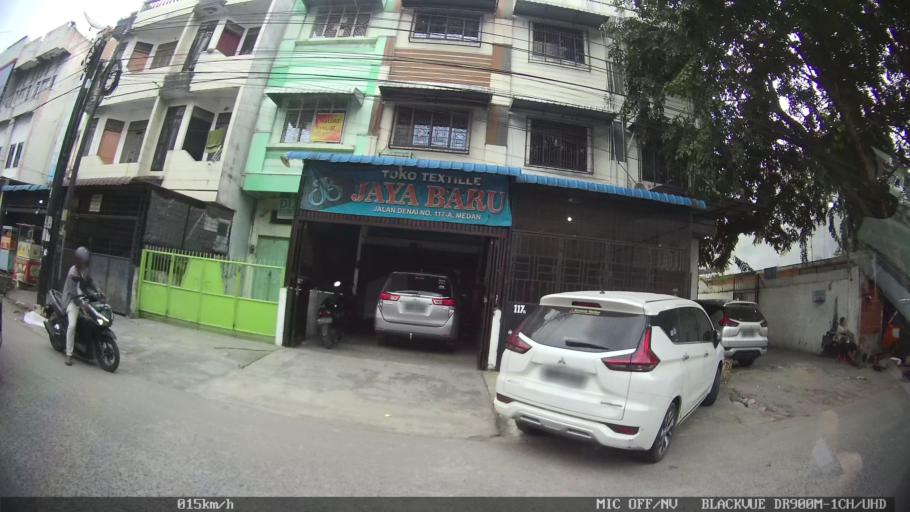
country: ID
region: North Sumatra
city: Medan
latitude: 3.5819
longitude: 98.7065
